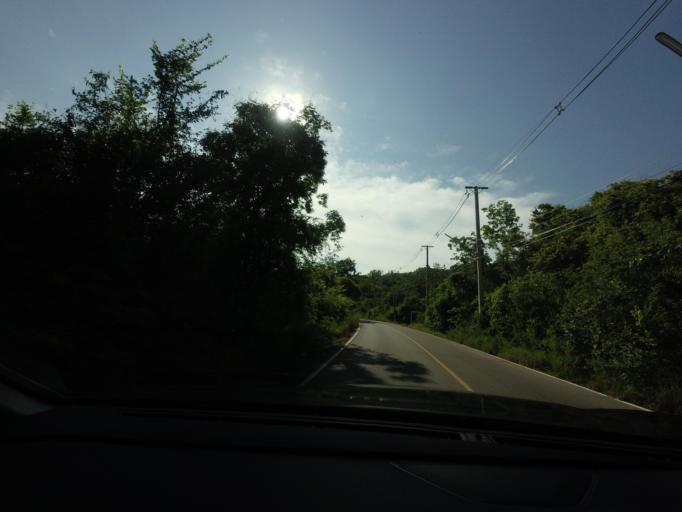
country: TH
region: Prachuap Khiri Khan
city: Pran Buri
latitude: 12.4114
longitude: 99.9745
